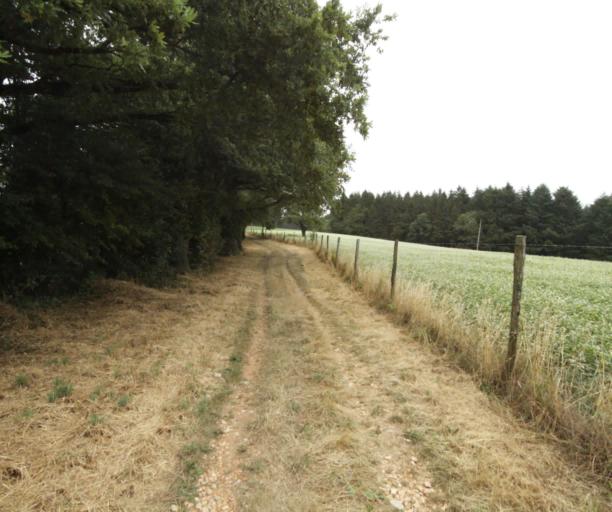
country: FR
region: Midi-Pyrenees
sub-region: Departement du Tarn
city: Soreze
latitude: 43.4043
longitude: 2.0710
